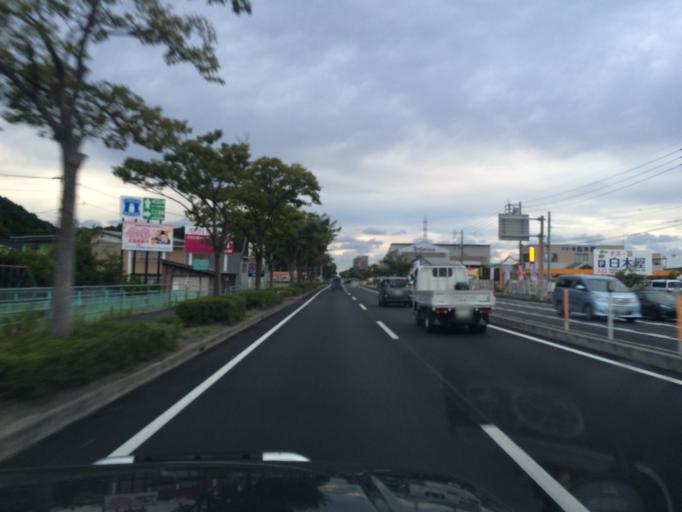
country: JP
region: Tottori
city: Tottori
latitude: 35.4913
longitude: 134.2037
